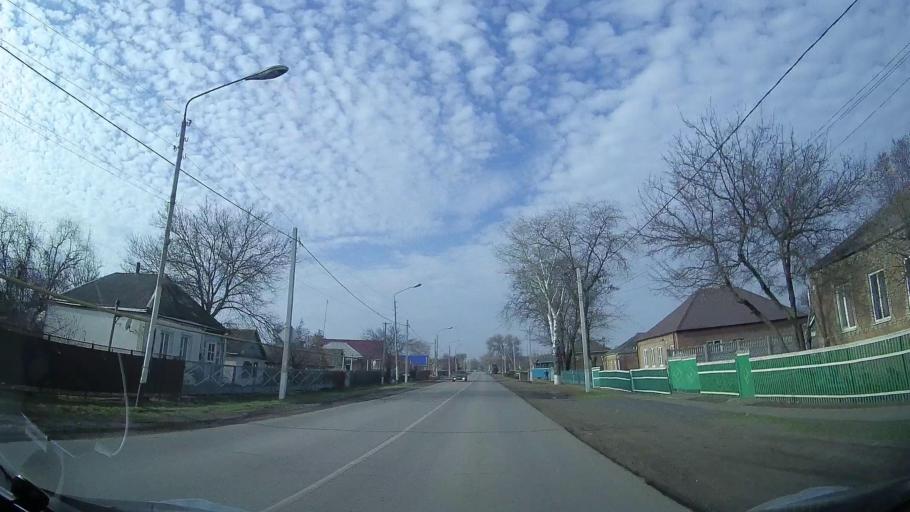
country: RU
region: Rostov
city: Veselyy
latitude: 47.0885
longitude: 40.7526
